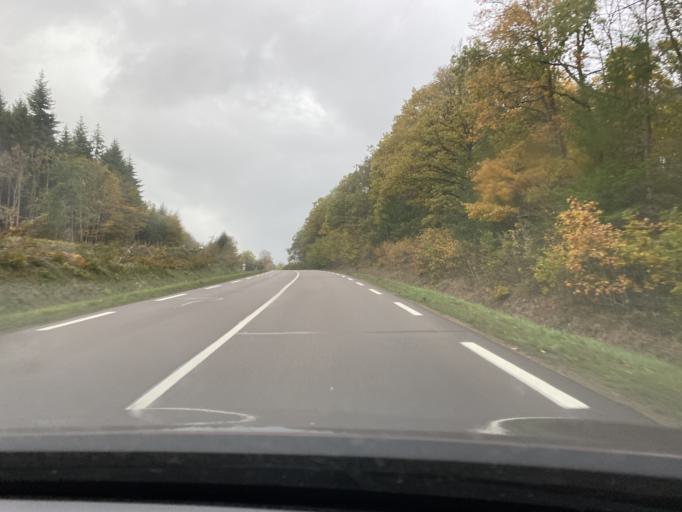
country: FR
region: Bourgogne
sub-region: Departement de la Cote-d'Or
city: Saulieu
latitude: 47.3061
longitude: 4.2086
